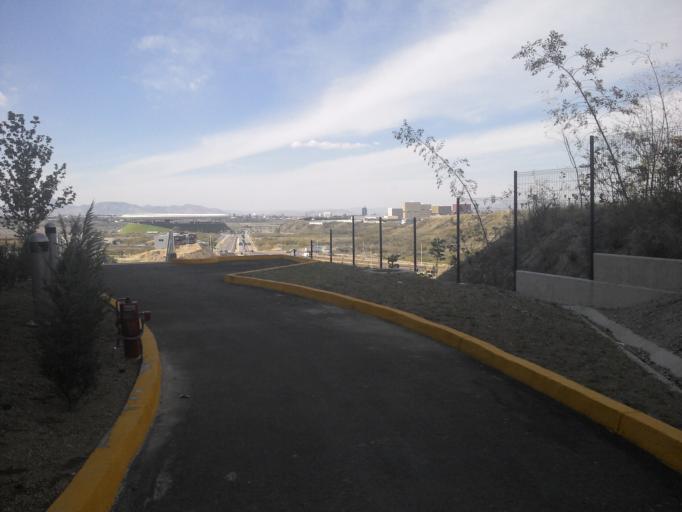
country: MX
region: Jalisco
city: Guadalajara
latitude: 20.6690
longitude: -103.4622
